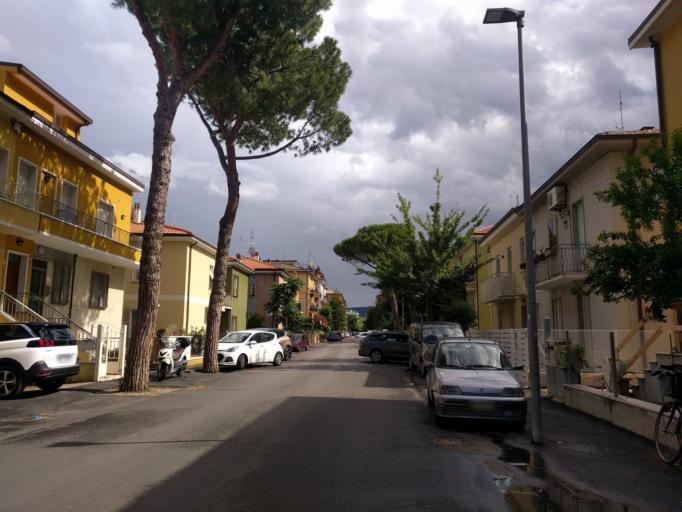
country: IT
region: The Marches
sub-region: Provincia di Pesaro e Urbino
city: Pesaro
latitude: 43.9007
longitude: 12.9091
